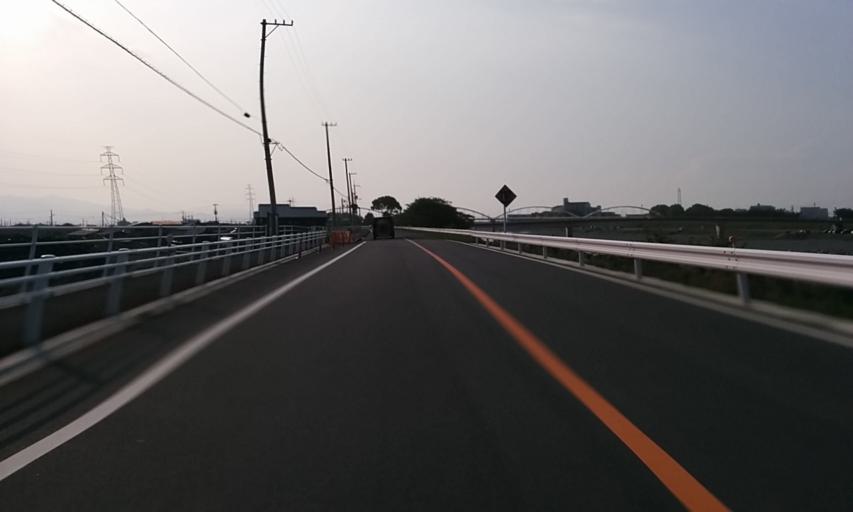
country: JP
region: Ehime
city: Saijo
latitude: 33.8980
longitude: 133.1914
